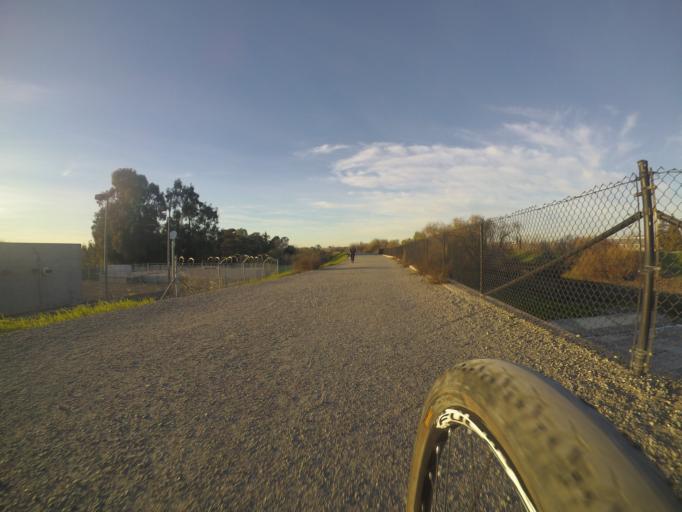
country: US
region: California
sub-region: Santa Clara County
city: Santa Clara
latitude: 37.4047
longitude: -121.9526
